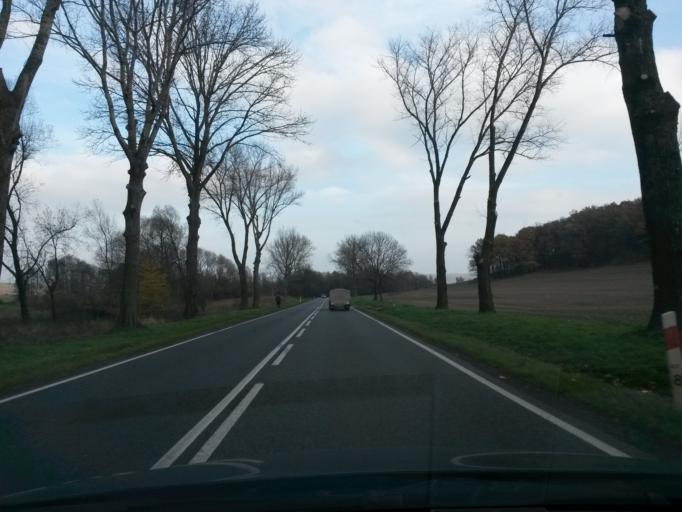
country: PL
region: Lower Silesian Voivodeship
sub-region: Powiat jaworski
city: Bolkow
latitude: 50.9159
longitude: 16.1160
